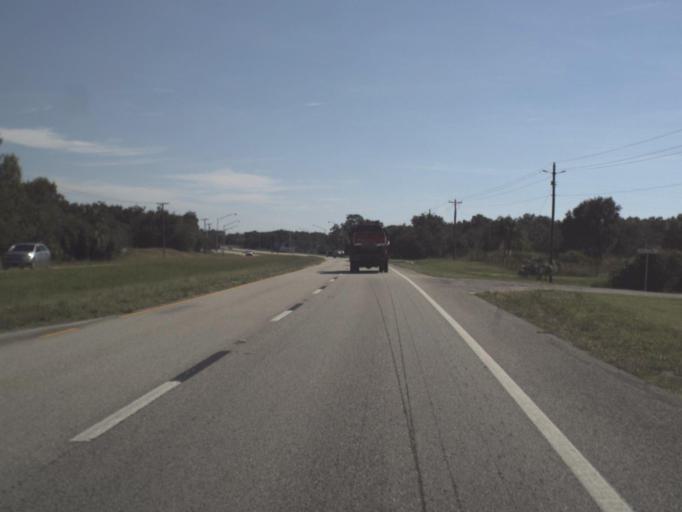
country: US
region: Florida
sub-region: Highlands County
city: Sebring
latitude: 27.3957
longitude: -81.4161
